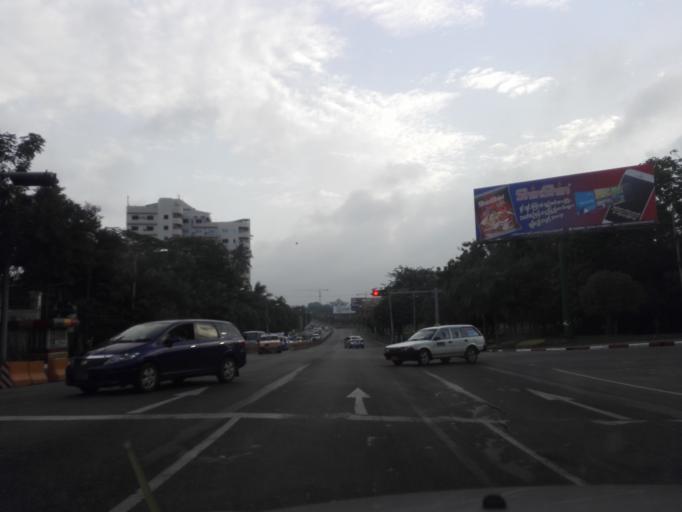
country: MM
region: Yangon
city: Yangon
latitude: 16.8345
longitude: 96.1334
